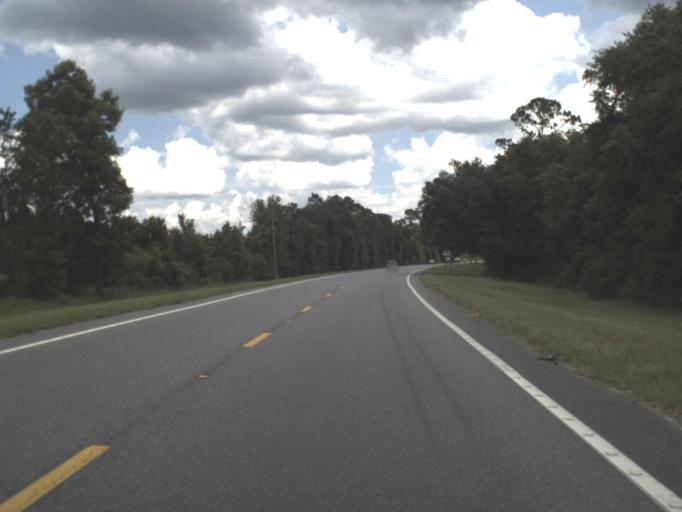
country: US
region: Florida
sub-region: Taylor County
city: Perry
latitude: 30.0917
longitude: -83.4928
